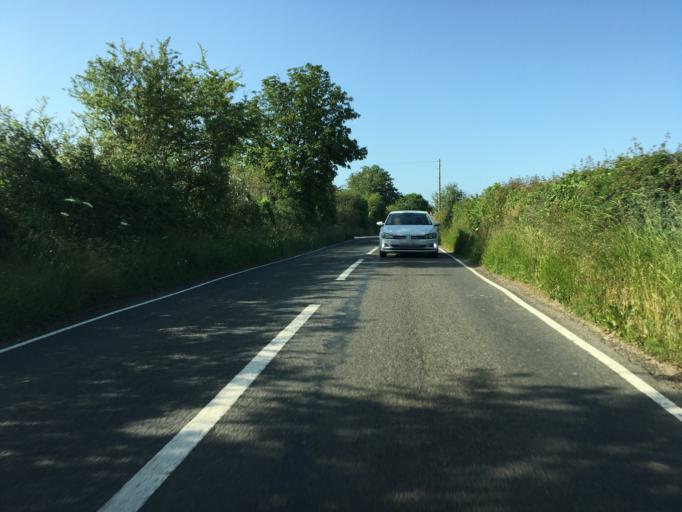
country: GB
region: England
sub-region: Oxfordshire
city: Charlbury
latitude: 51.8844
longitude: -1.4750
